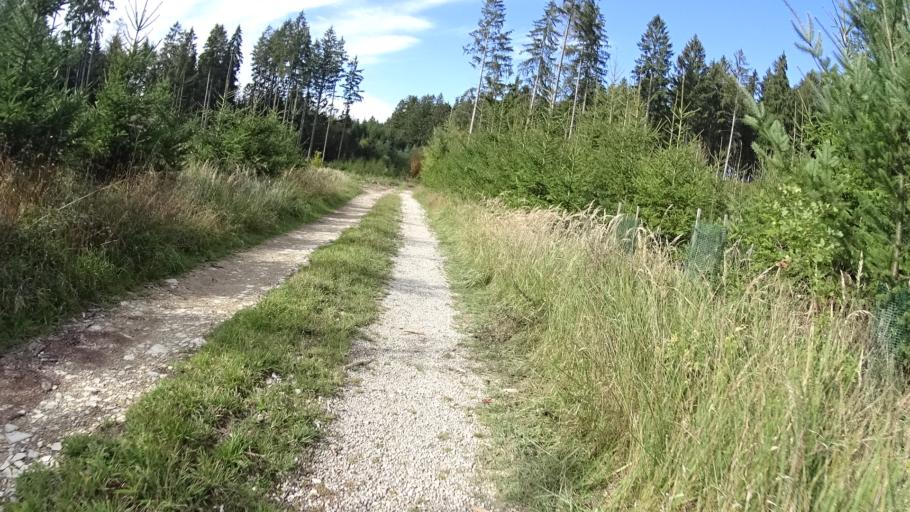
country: DE
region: Bavaria
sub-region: Upper Bavaria
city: Bohmfeld
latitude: 48.8814
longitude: 11.3803
